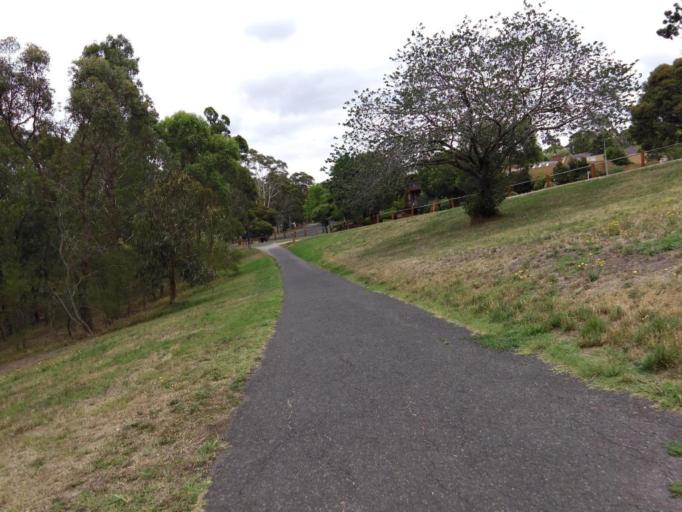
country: AU
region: Victoria
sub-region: Manningham
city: Doncaster
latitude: -37.7748
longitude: 145.1335
